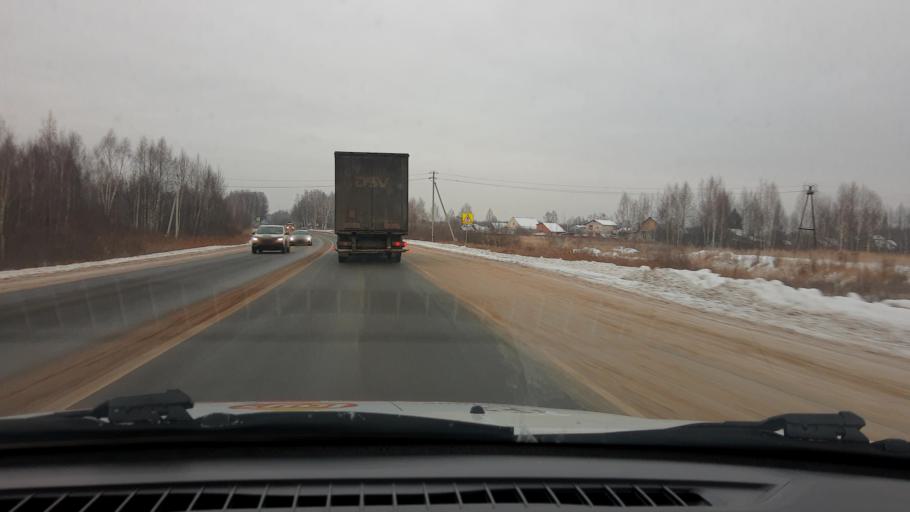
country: RU
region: Nizjnij Novgorod
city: Sitniki
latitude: 56.5250
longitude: 44.0264
